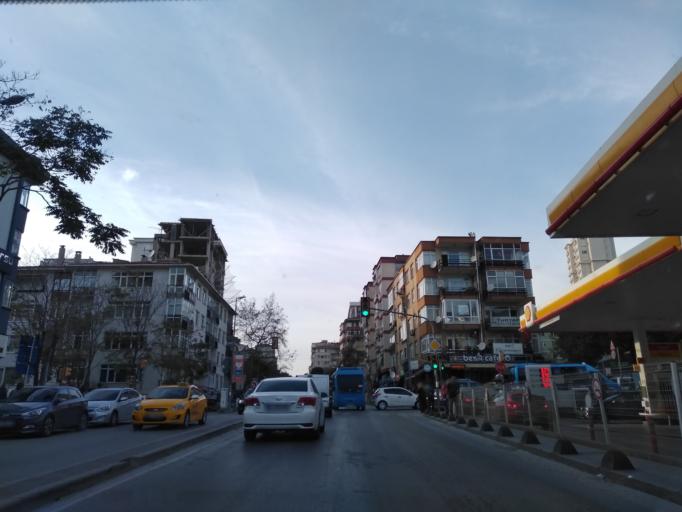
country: TR
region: Istanbul
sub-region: Atasehir
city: Atasehir
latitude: 40.9572
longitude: 29.0977
